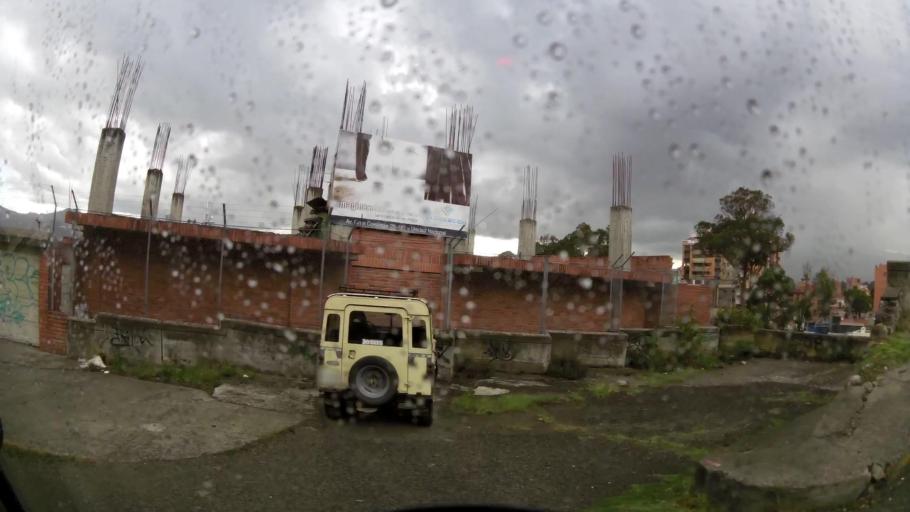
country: EC
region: Azuay
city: Cuenca
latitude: -2.8914
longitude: -79.0196
